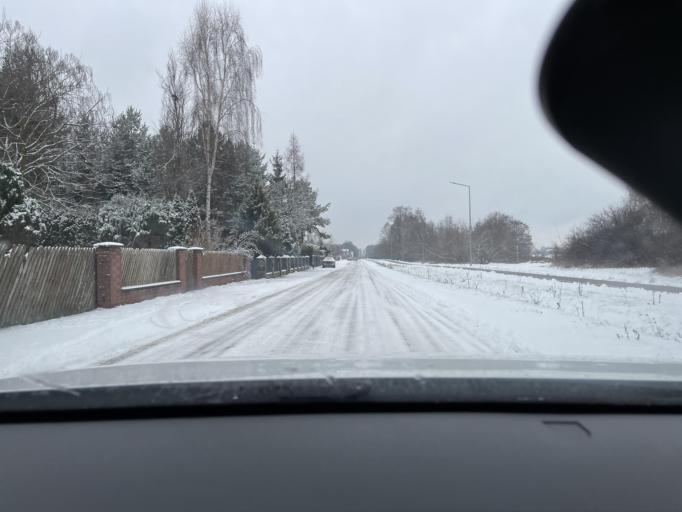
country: PL
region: Masovian Voivodeship
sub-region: Powiat zyrardowski
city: Zyrardow
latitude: 52.0327
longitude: 20.4561
